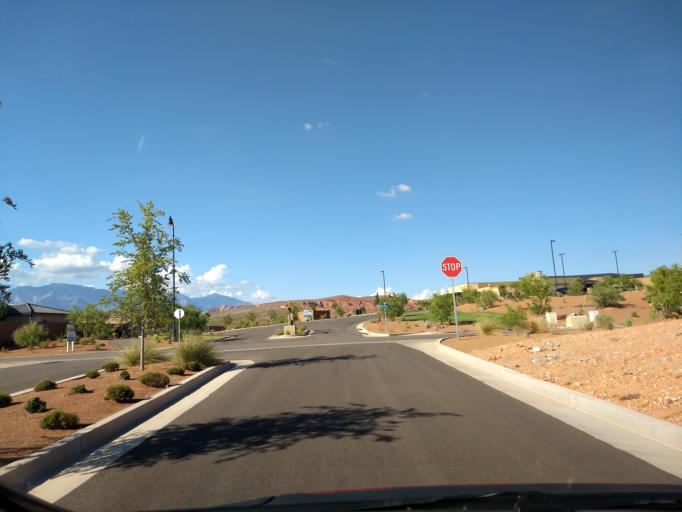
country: US
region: Utah
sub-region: Washington County
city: Washington
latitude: 37.1421
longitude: -113.5149
